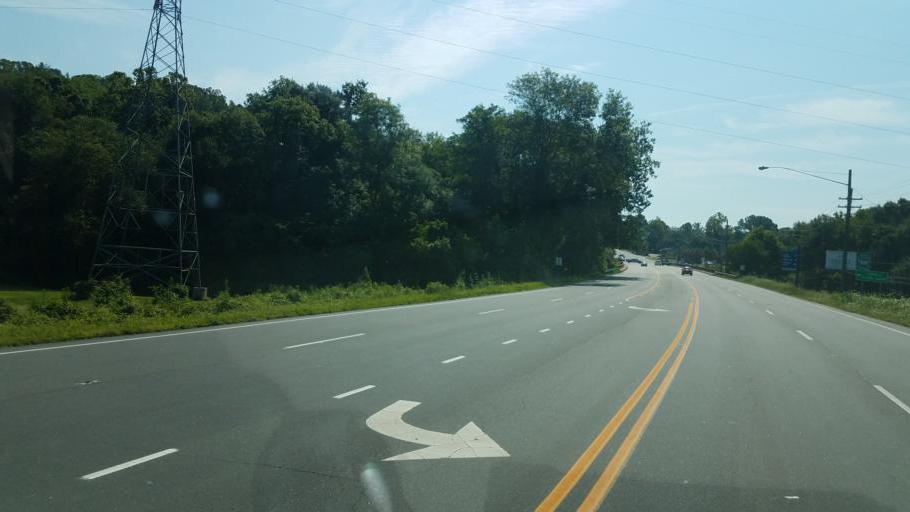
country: US
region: North Carolina
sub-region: Burke County
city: Morganton
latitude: 35.7503
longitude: -81.7075
